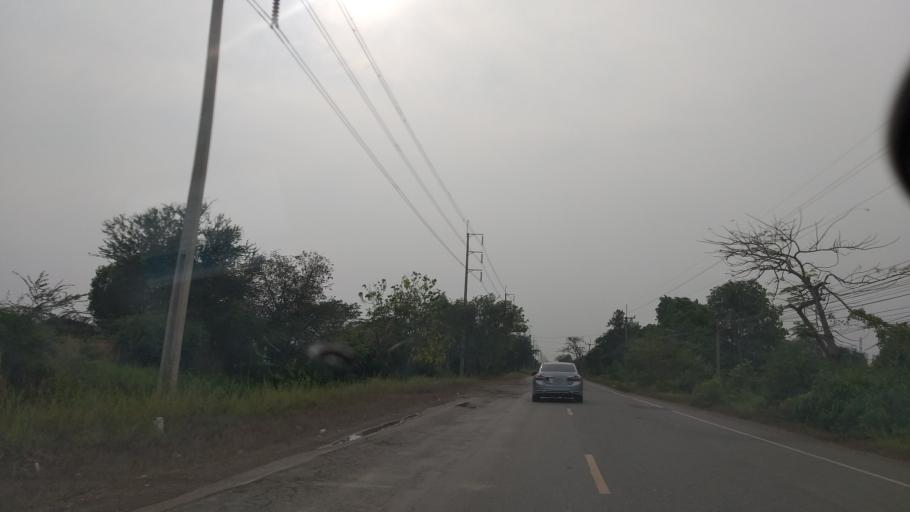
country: TH
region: Chachoengsao
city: Ban Pho
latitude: 13.5991
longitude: 101.1750
